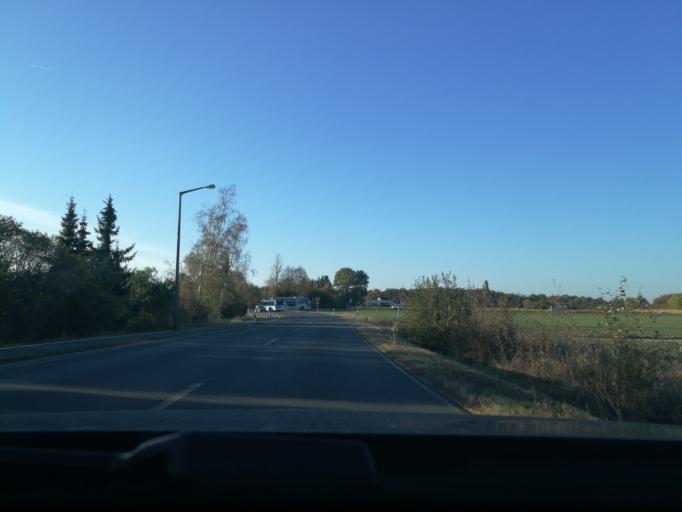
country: DE
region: Bavaria
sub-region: Regierungsbezirk Mittelfranken
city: Erlangen
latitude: 49.5332
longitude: 11.0294
